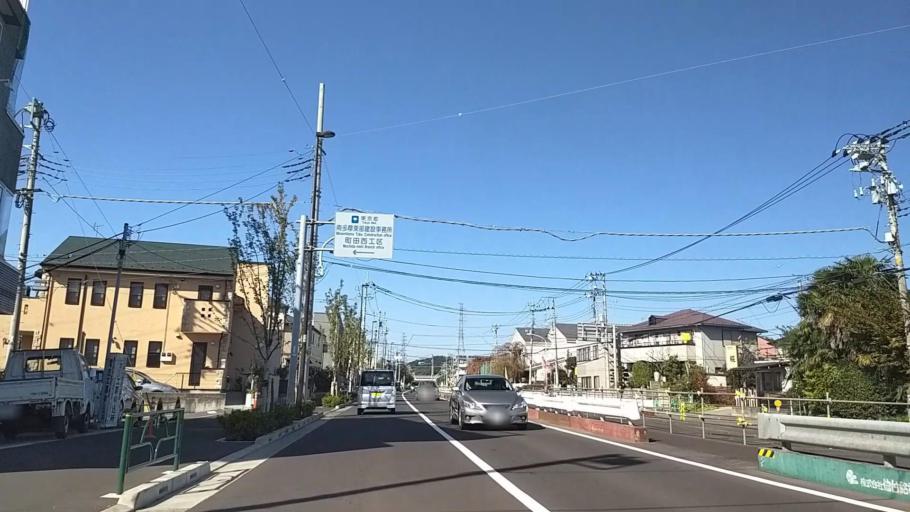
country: JP
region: Tokyo
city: Hachioji
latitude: 35.5964
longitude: 139.3699
